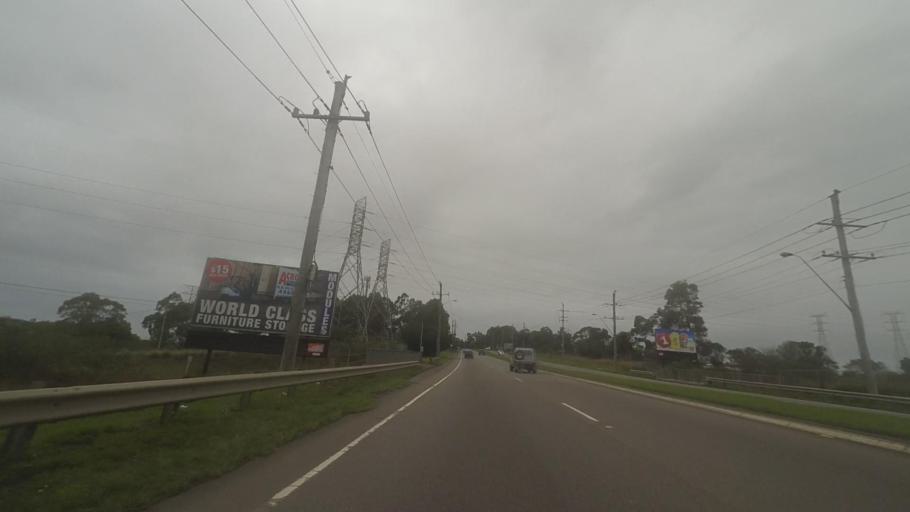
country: AU
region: New South Wales
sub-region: Newcastle
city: Mayfield West
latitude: -32.8761
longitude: 151.7136
